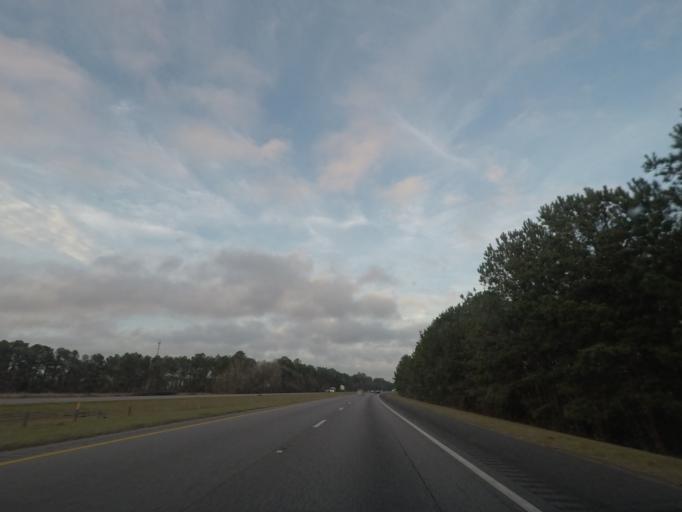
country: US
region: South Carolina
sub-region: Orangeburg County
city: Holly Hill
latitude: 33.3976
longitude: -80.5126
